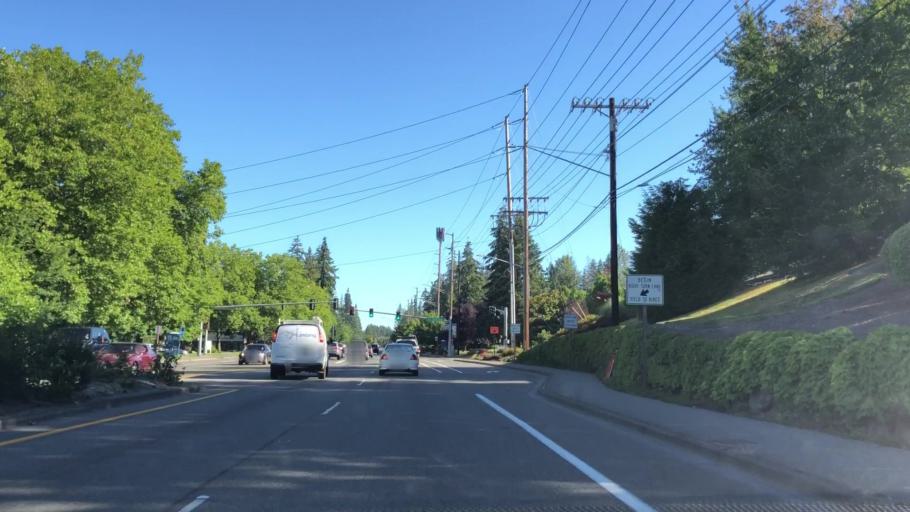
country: US
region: Washington
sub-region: Snohomish County
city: Mill Creek
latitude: 47.8539
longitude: -122.2182
